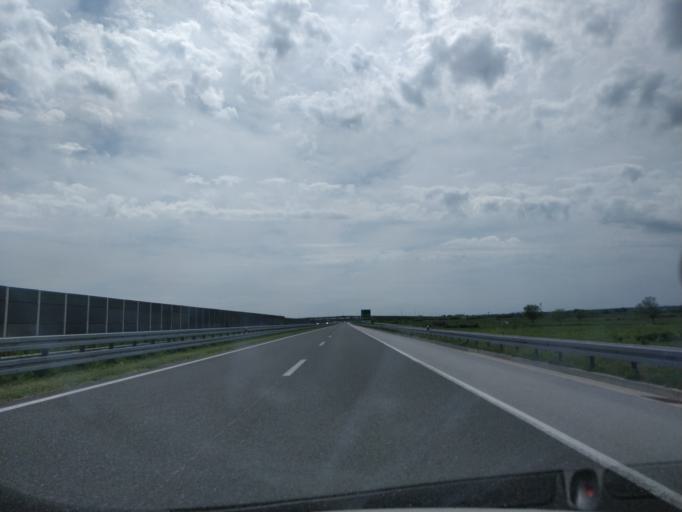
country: HR
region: Zagrebacka
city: Gradici
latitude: 45.7052
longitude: 16.0502
